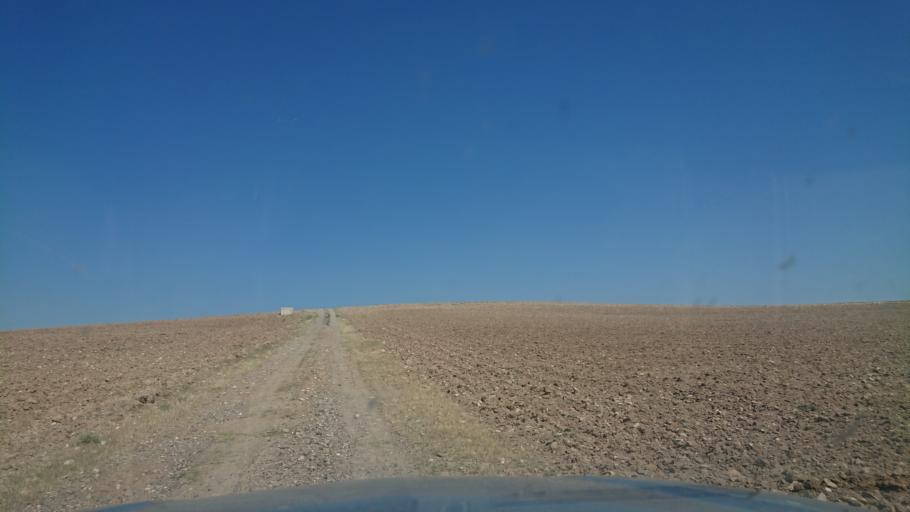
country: TR
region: Aksaray
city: Sariyahsi
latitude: 39.0540
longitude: 33.8887
